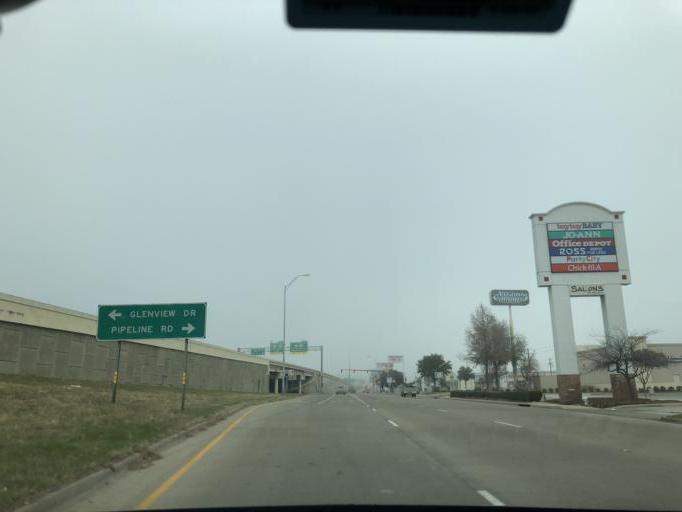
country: US
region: Texas
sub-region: Tarrant County
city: Richland Hills
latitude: 32.8222
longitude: -97.2051
